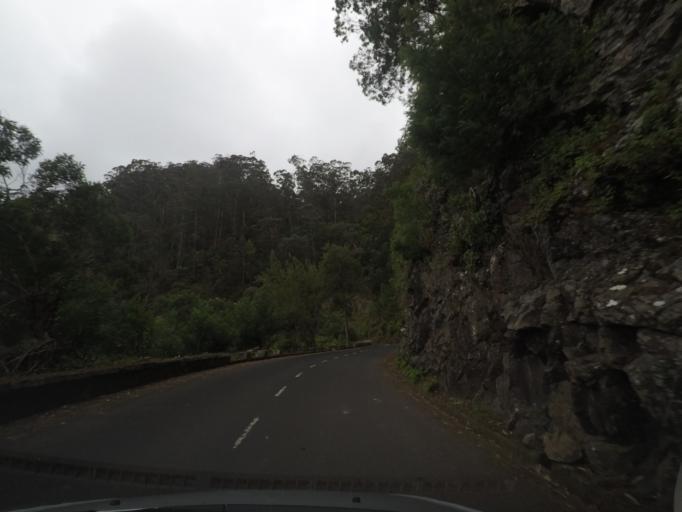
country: PT
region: Madeira
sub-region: Santana
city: Santana
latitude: 32.7510
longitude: -16.8362
